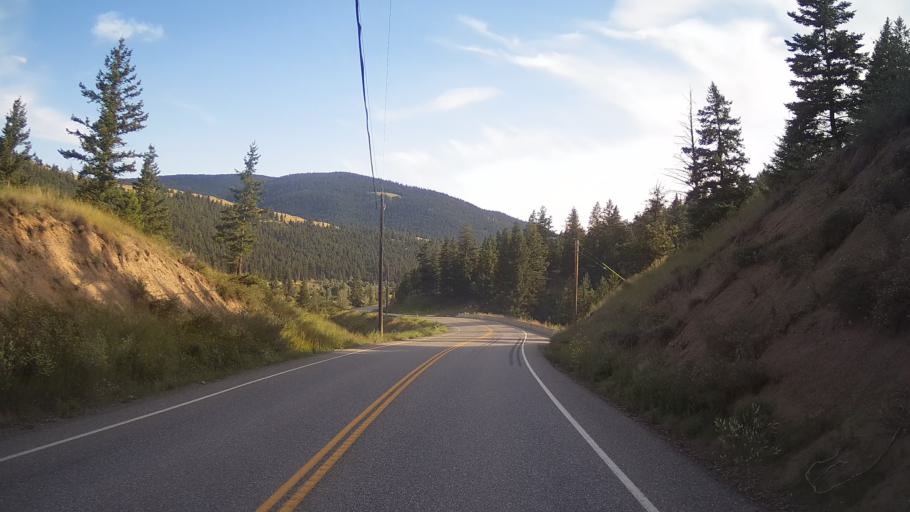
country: CA
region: British Columbia
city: Cache Creek
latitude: 50.8454
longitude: -121.5400
